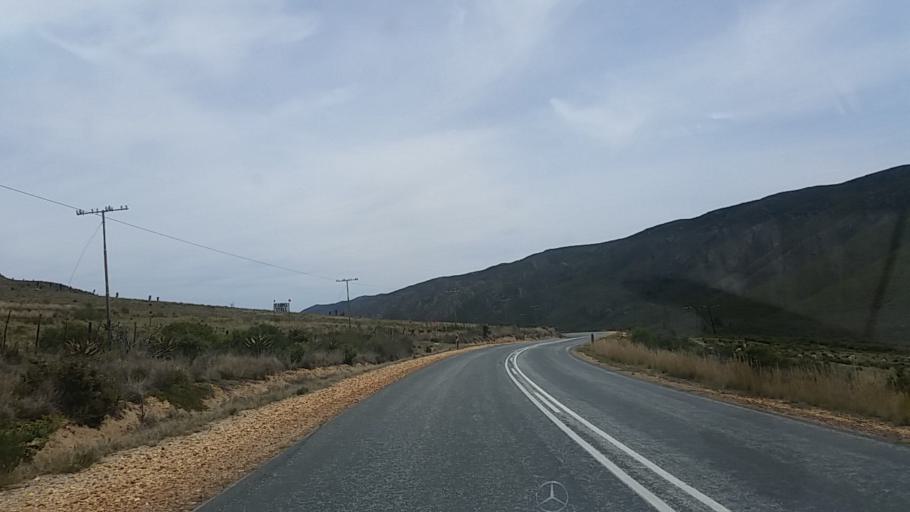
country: ZA
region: Western Cape
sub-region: Eden District Municipality
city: Knysna
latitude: -33.7427
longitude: 23.0056
